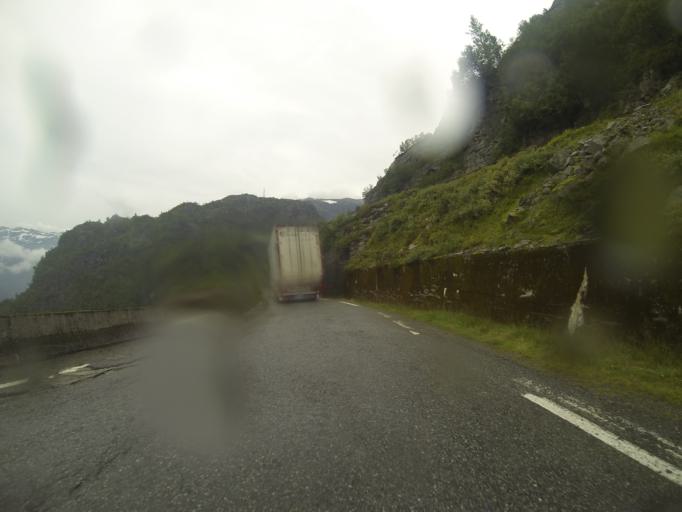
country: NO
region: Hordaland
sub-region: Odda
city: Odda
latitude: 59.7861
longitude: 6.7560
